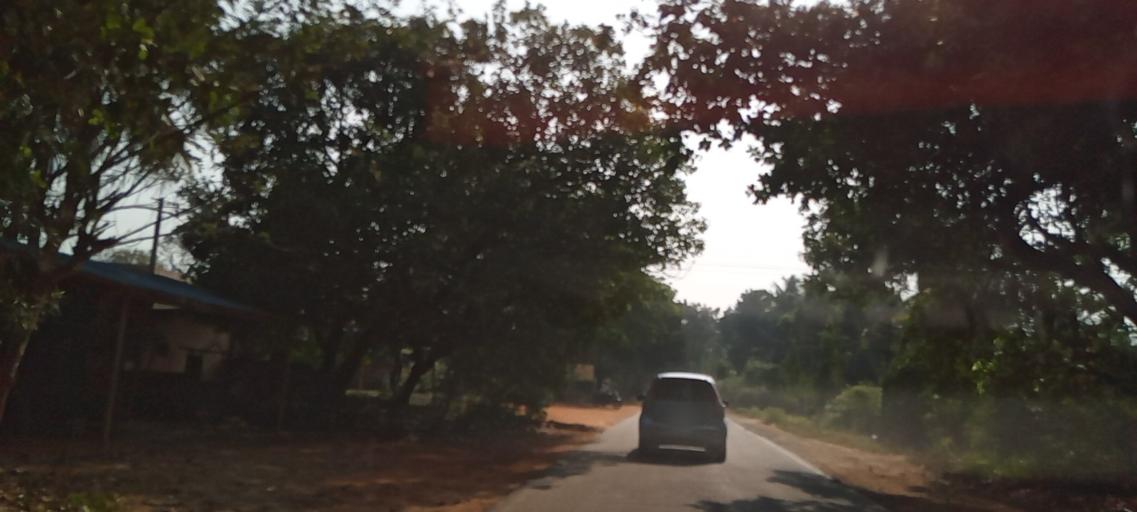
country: IN
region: Karnataka
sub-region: Udupi
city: Coondapoor
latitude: 13.5120
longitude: 74.7763
